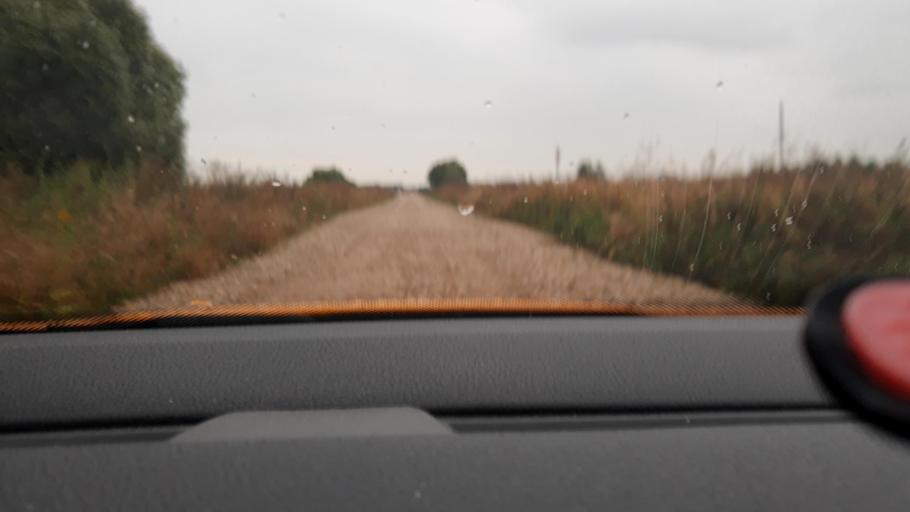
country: RU
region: Moskovskaya
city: Obukhovo
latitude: 55.8042
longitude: 38.2822
